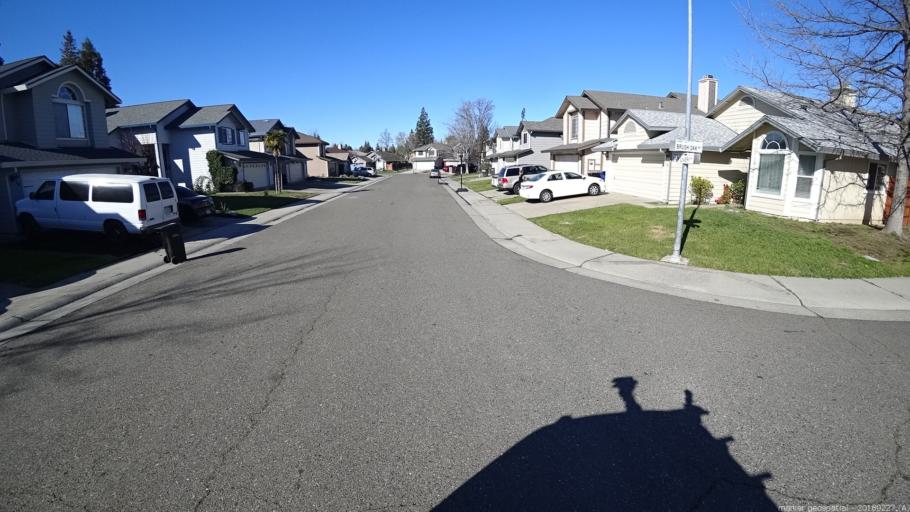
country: US
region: California
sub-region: Sacramento County
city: North Highlands
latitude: 38.7185
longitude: -121.3713
